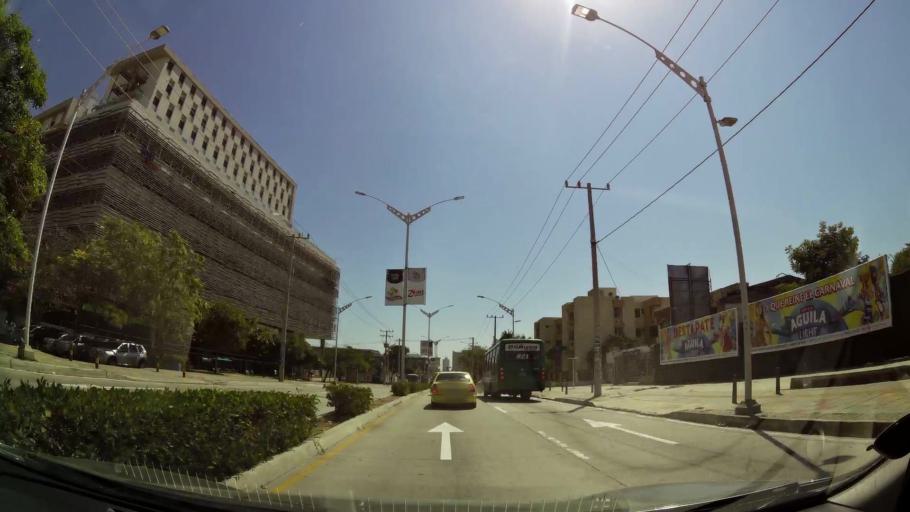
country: CO
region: Atlantico
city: Barranquilla
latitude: 11.0101
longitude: -74.8266
